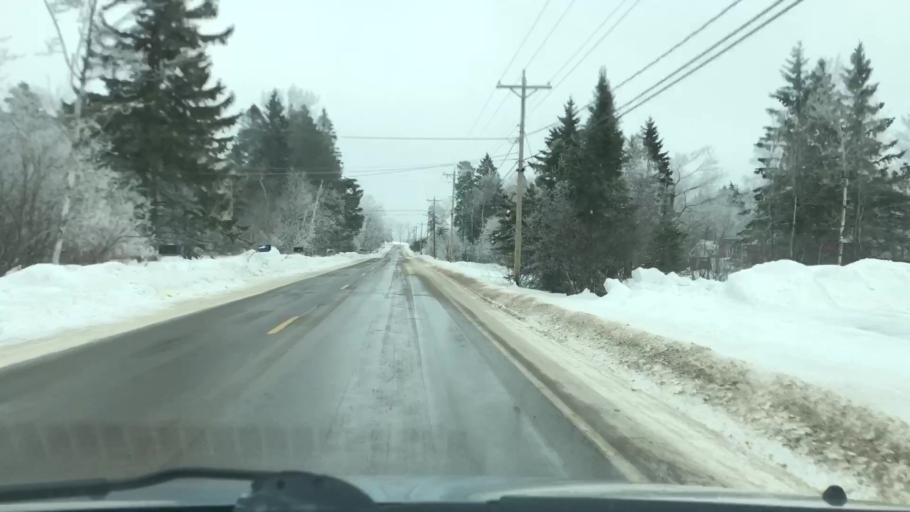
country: US
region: Minnesota
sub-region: Saint Louis County
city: Arnold
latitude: 46.8595
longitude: -92.1179
